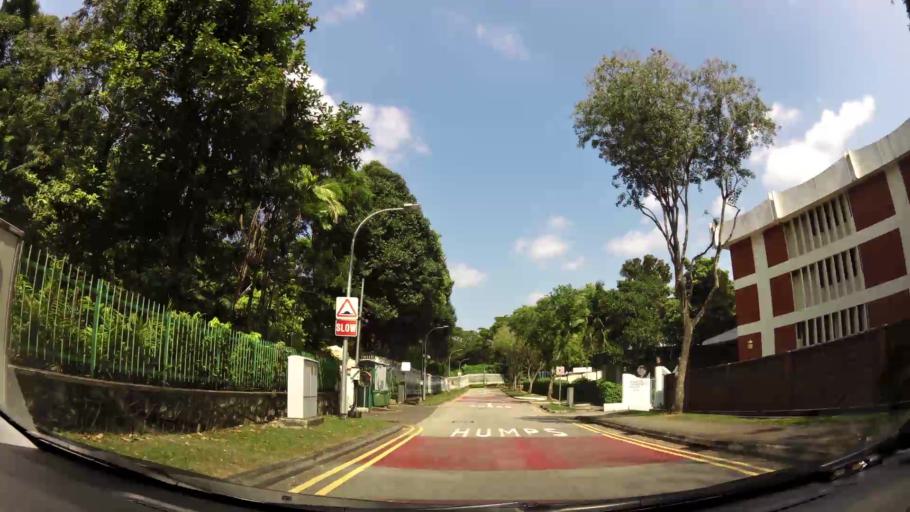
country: SG
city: Singapore
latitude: 1.3031
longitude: 103.8459
